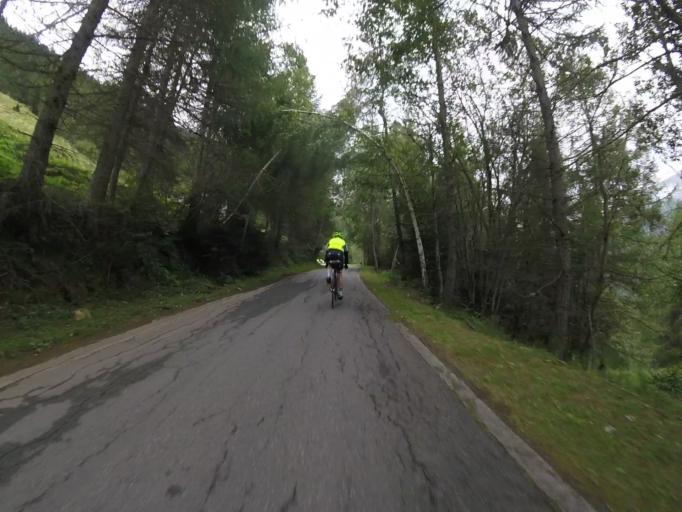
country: IT
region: Lombardy
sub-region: Provincia di Brescia
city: Monno
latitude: 46.2374
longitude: 10.3202
